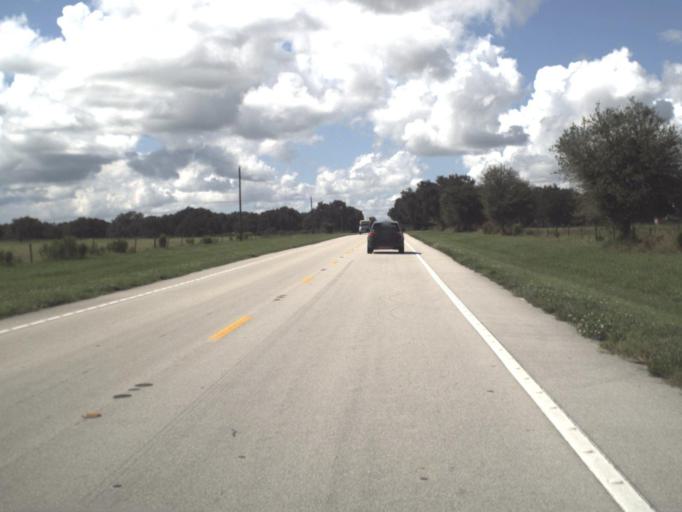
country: US
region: Florida
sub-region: DeSoto County
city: Arcadia
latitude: 27.2739
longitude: -82.0126
